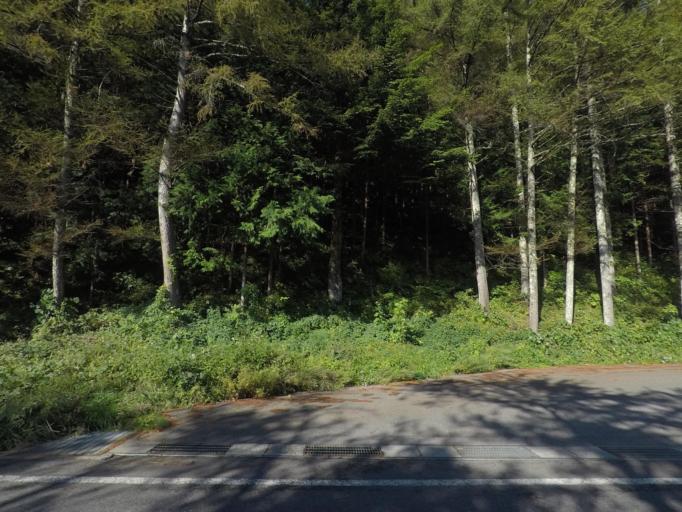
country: JP
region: Nagano
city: Ina
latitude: 35.9618
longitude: 137.7662
